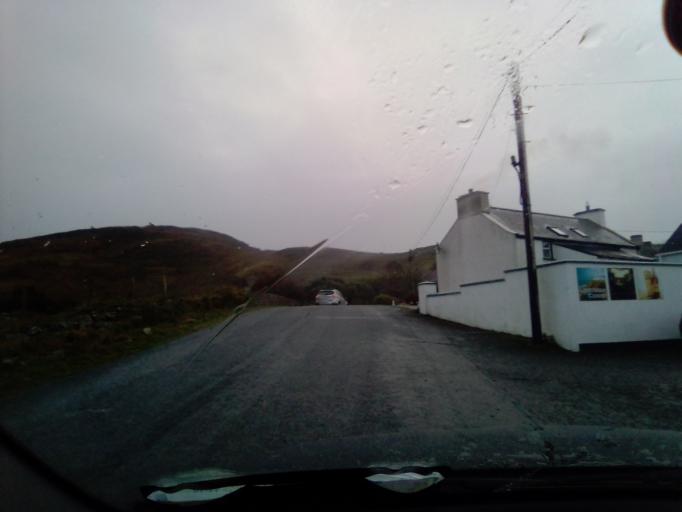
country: IE
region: Ulster
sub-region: County Donegal
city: Ramelton
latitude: 55.2702
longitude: -7.6405
